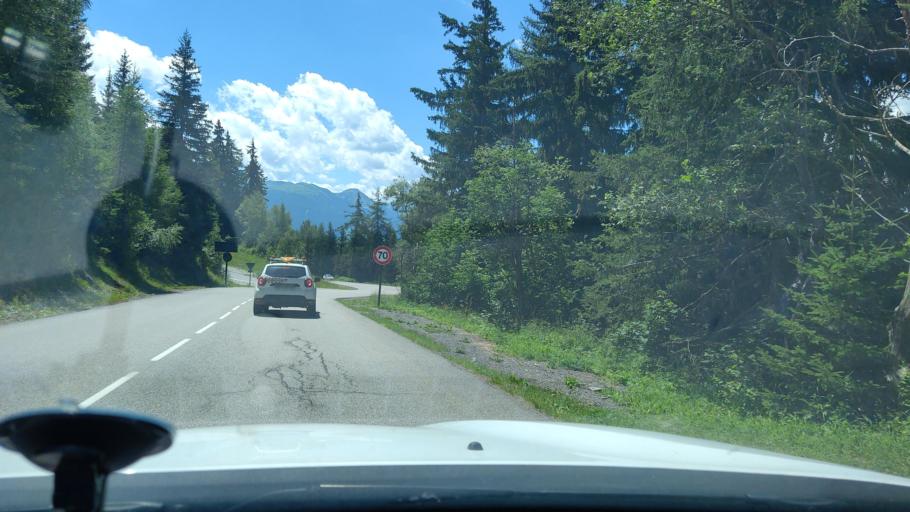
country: FR
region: Rhone-Alpes
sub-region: Departement de la Savoie
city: Seez
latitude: 45.6014
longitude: 6.7977
